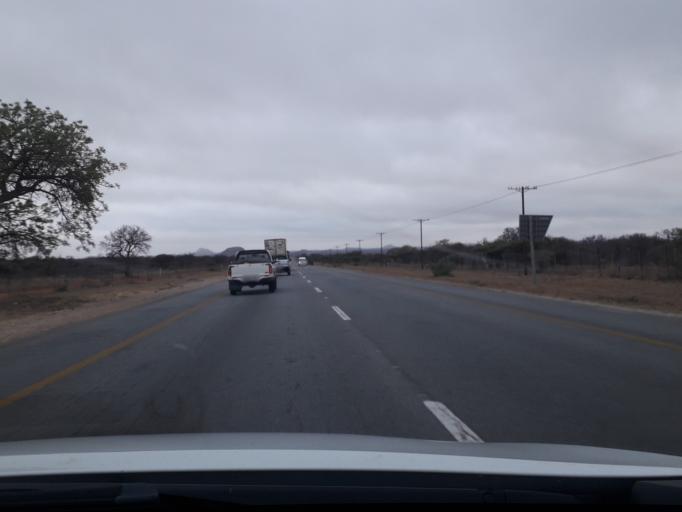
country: ZA
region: Limpopo
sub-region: Capricorn District Municipality
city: Mankoeng
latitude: -23.5752
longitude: 29.6730
